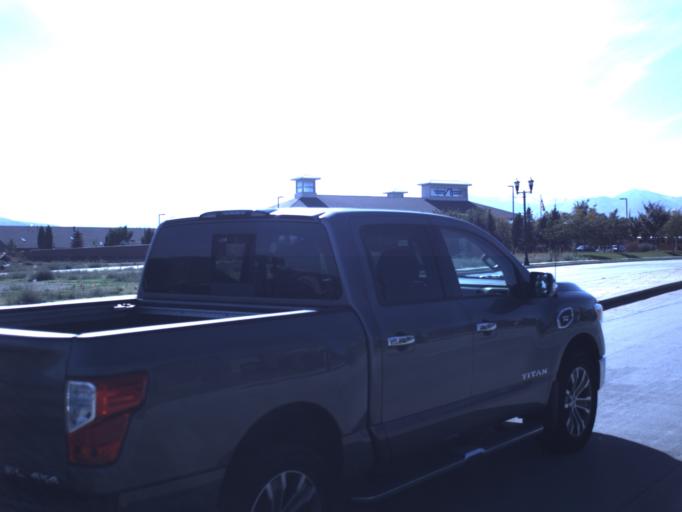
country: US
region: Utah
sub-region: Salt Lake County
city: South Jordan Heights
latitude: 40.5622
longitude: -111.9700
